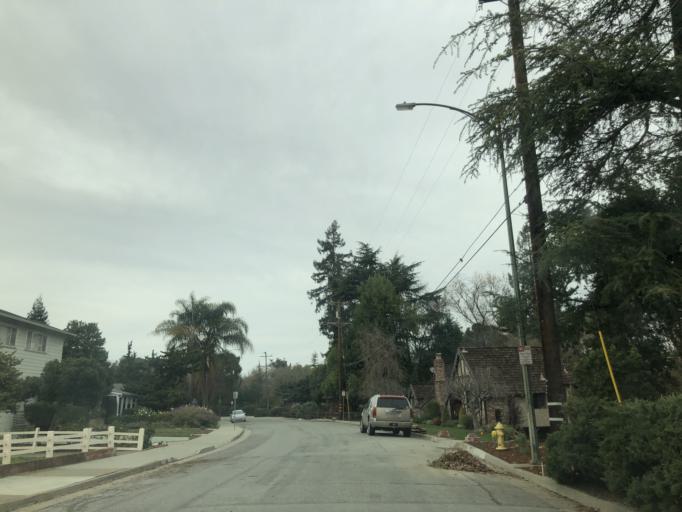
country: US
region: California
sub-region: Santa Clara County
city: San Jose
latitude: 37.3414
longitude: -121.8713
